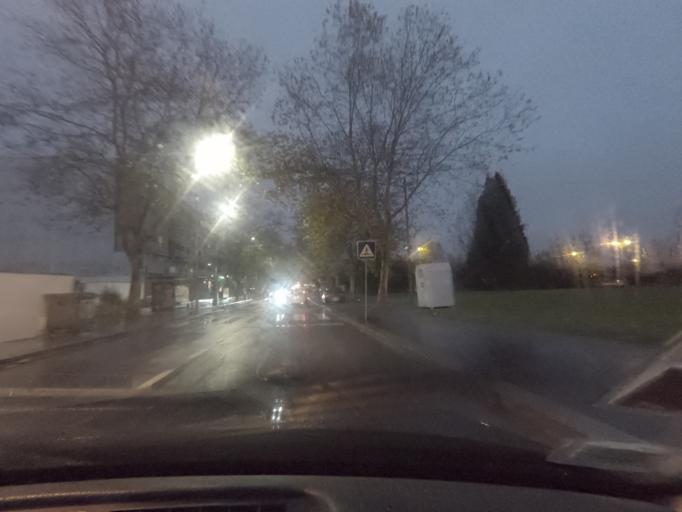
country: PT
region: Porto
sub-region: Matosinhos
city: Senhora da Hora
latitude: 41.1869
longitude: -8.6637
